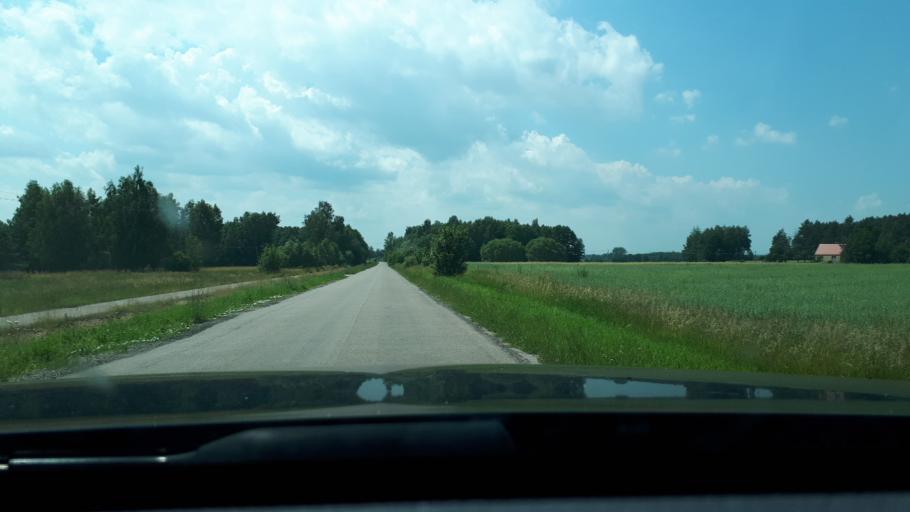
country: PL
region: Podlasie
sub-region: Powiat bialostocki
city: Choroszcz
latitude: 53.1212
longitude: 22.9096
